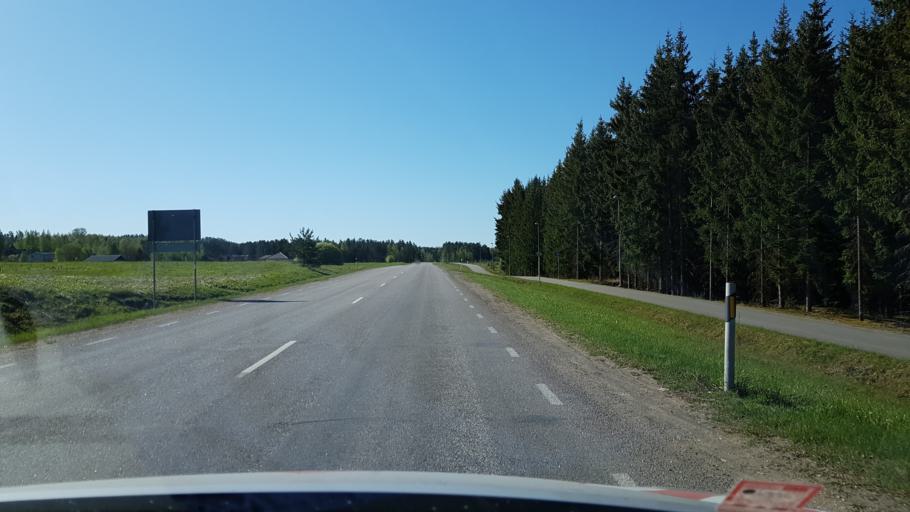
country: EE
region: Vorumaa
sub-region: Voru linn
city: Voru
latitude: 57.8122
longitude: 27.0306
